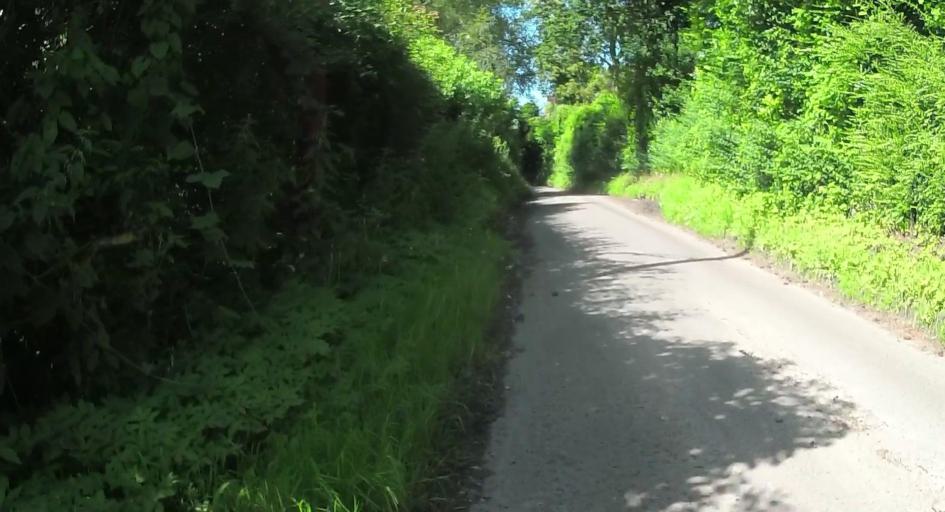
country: GB
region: England
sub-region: Hampshire
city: Kingsley
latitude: 51.1514
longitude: -0.8934
